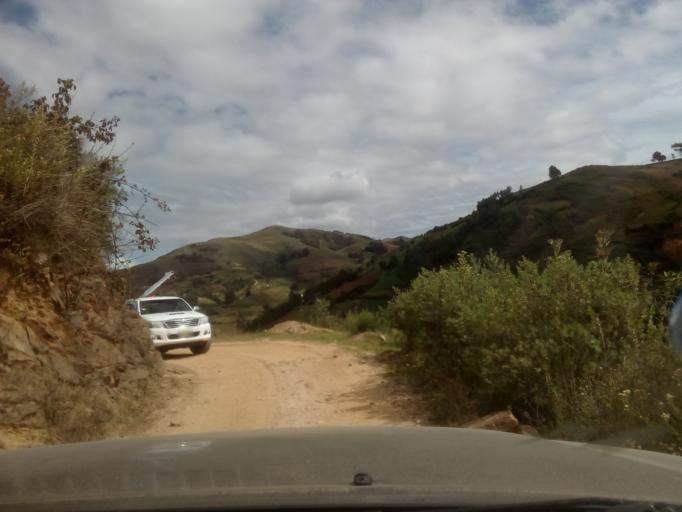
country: PE
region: La Libertad
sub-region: Sanchez Carrion
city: Curgos
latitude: -7.8707
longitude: -77.9587
